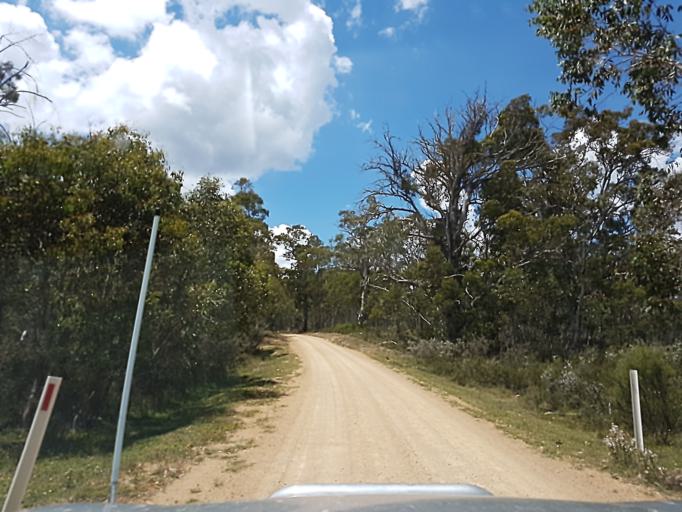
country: AU
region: New South Wales
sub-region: Snowy River
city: Jindabyne
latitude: -36.8779
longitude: 148.0737
